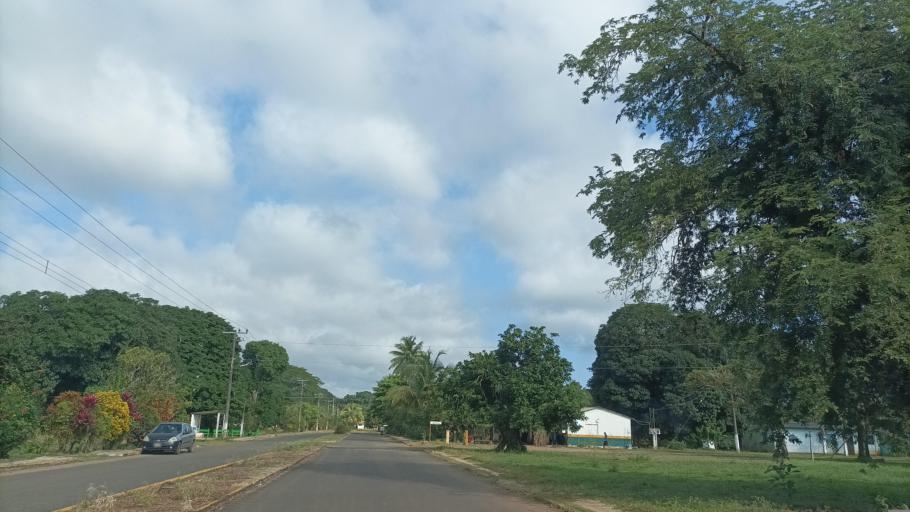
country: MX
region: Veracruz
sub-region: Pajapan
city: Pajapan
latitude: 18.1729
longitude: -94.6672
